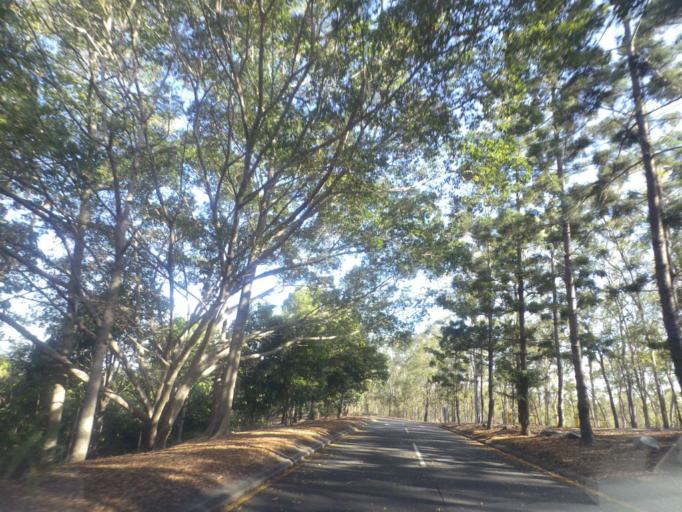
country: AU
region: Queensland
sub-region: Brisbane
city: Taringa
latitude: -27.4802
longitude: 152.9693
